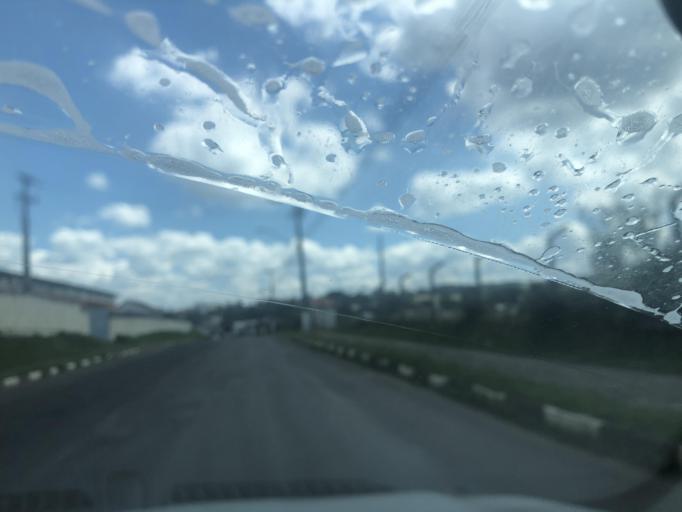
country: BR
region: Santa Catarina
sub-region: Lages
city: Lages
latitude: -27.7919
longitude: -50.3125
